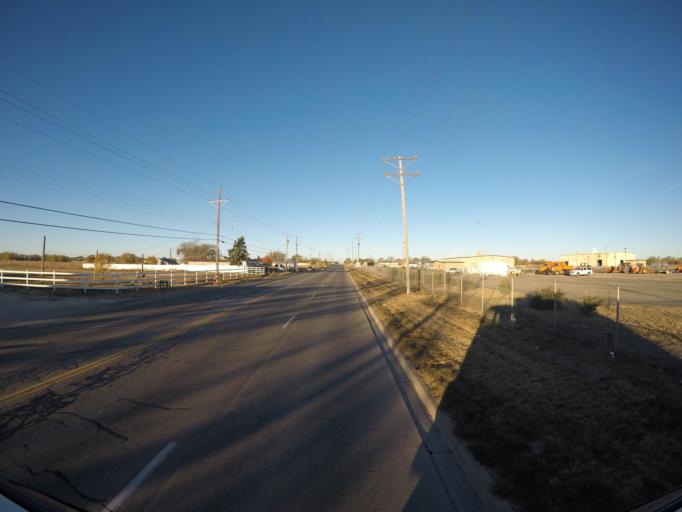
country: US
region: New Mexico
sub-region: Curry County
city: Clovis
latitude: 34.3902
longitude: -103.1899
